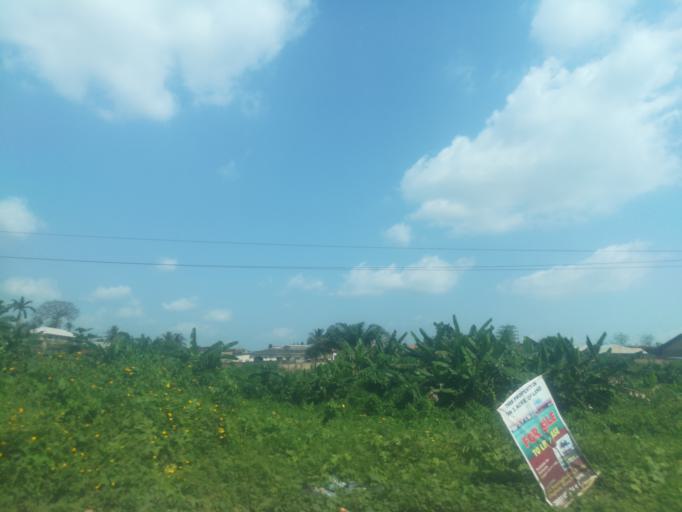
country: NG
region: Oyo
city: Moniya
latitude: 7.5085
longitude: 3.9127
